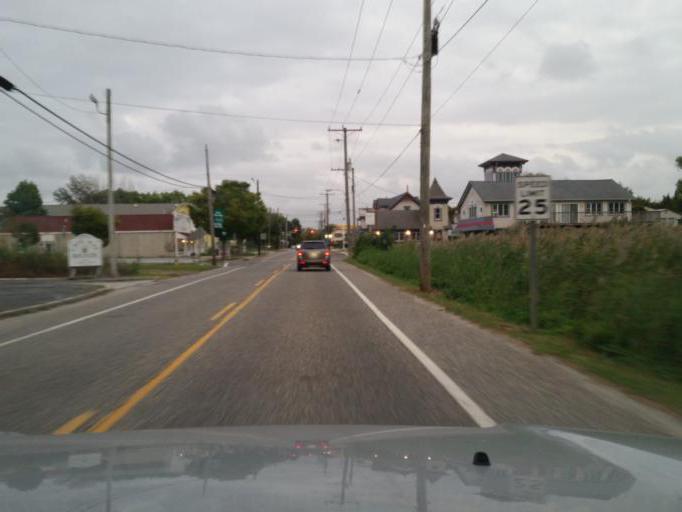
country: US
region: New Jersey
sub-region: Cape May County
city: West Cape May
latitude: 38.9358
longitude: -74.9336
